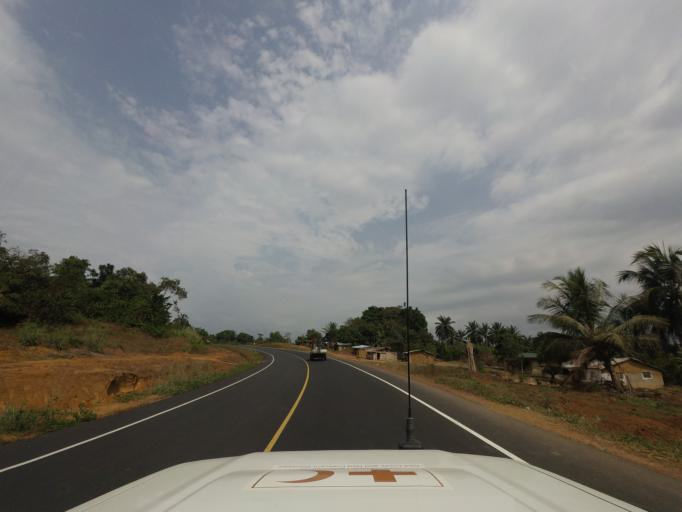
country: LR
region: Montserrado
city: Bensonville City
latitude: 6.3964
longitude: -10.4947
